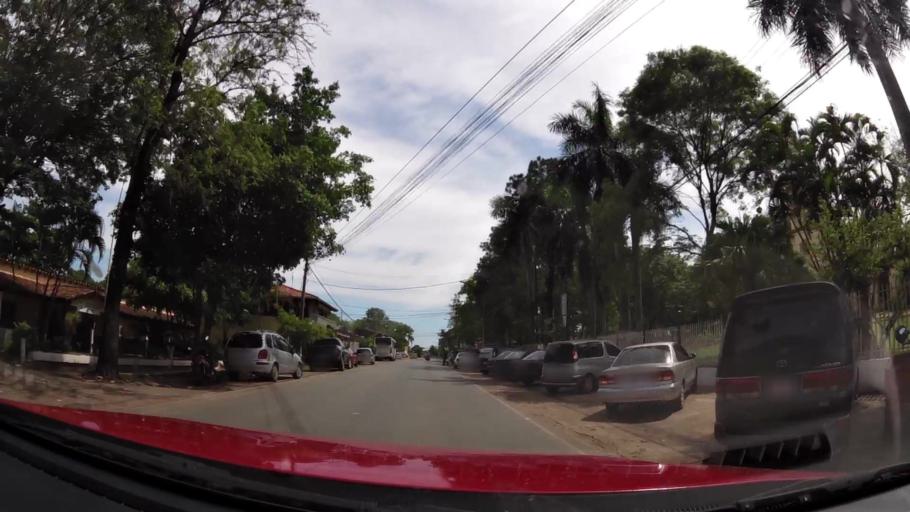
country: PY
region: Central
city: Limpio
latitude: -25.1655
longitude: -57.4749
